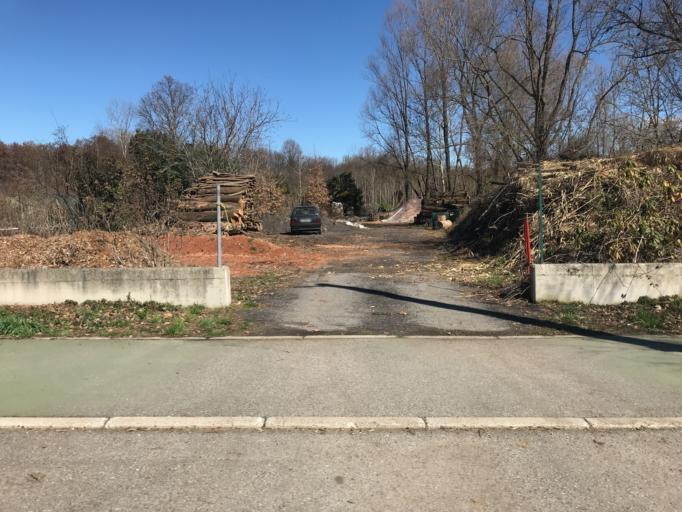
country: IT
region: Lombardy
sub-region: Provincia di Varese
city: Ranco
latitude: 45.7936
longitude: 8.5904
